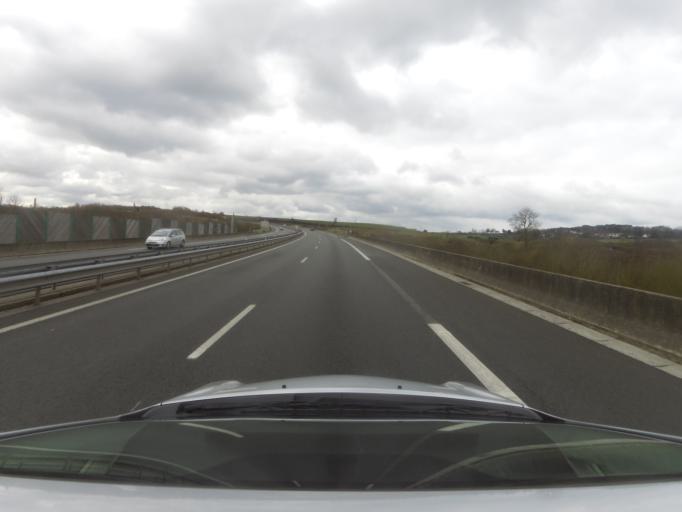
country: FR
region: Nord-Pas-de-Calais
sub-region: Departement du Pas-de-Calais
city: Isques
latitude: 50.6661
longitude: 1.6569
